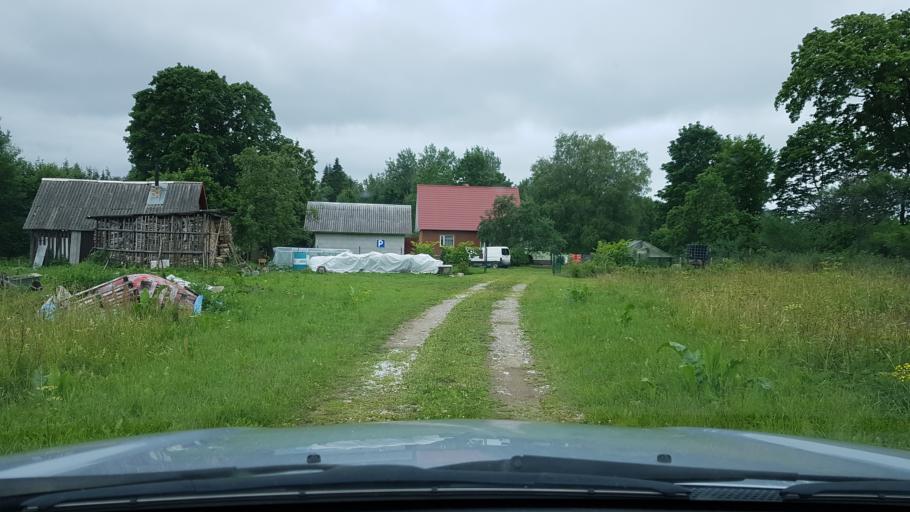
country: EE
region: Ida-Virumaa
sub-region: Narva-Joesuu linn
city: Narva-Joesuu
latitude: 59.3602
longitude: 28.0393
